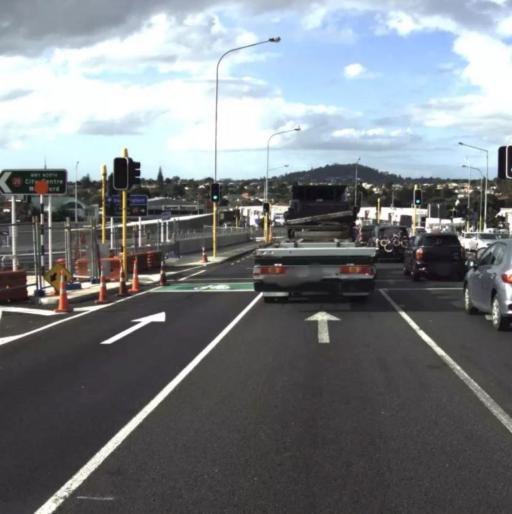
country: NZ
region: Auckland
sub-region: Auckland
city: Auckland
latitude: -36.9041
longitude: 174.7227
